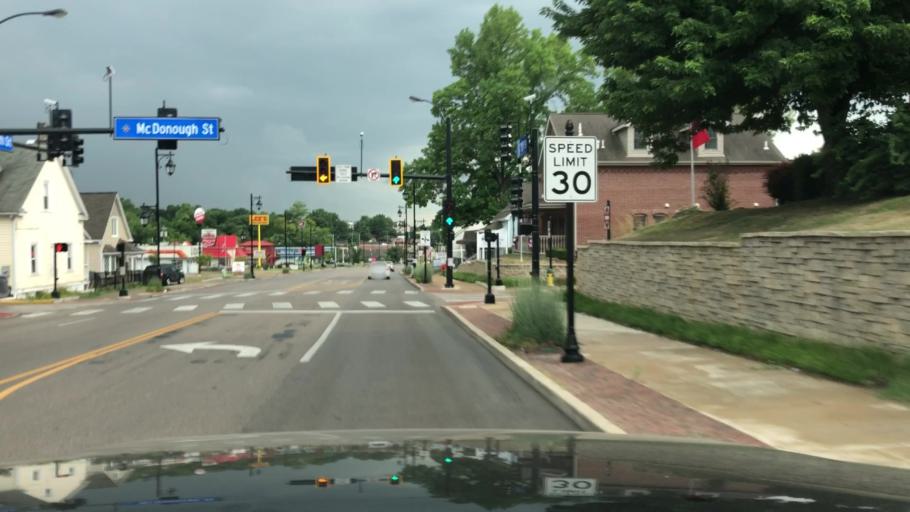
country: US
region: Missouri
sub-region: Saint Charles County
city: Saint Charles
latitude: 38.7767
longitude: -90.4893
